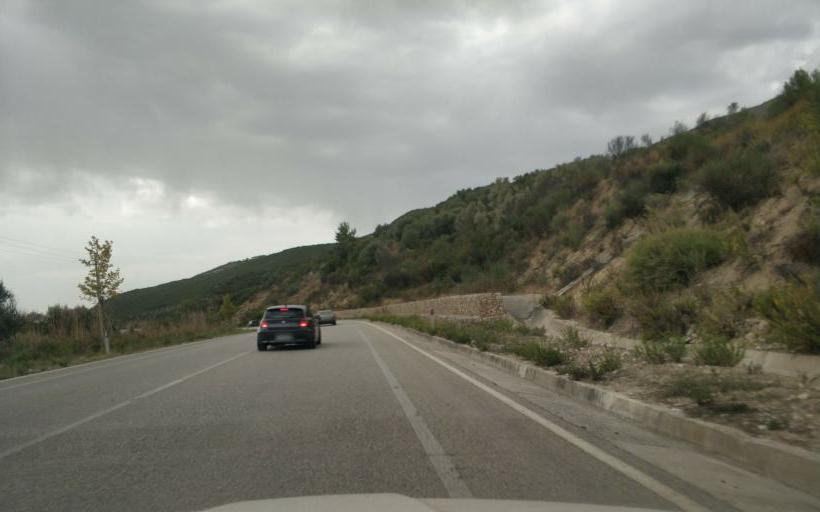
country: AL
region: Fier
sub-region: Rrethi i Mallakastres
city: Hekal
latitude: 40.5238
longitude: 19.7382
